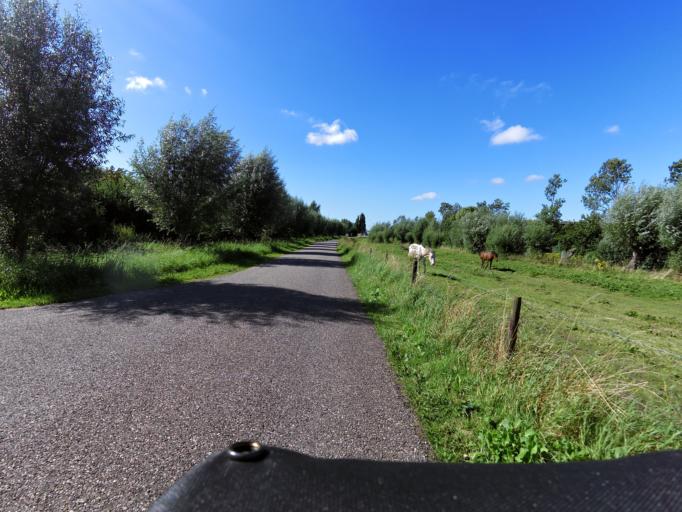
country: NL
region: South Holland
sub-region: Gemeente Spijkenisse
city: Spijkenisse
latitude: 51.8515
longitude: 4.2967
